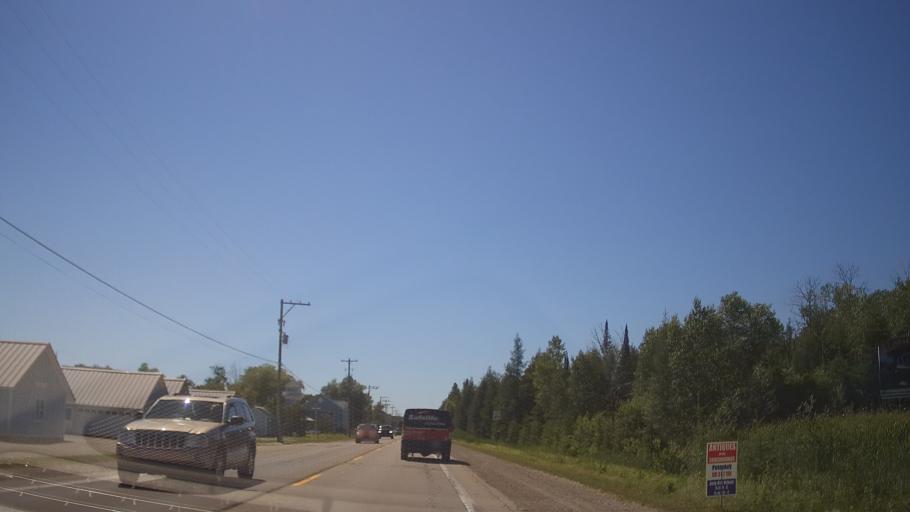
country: US
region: Michigan
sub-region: Emmet County
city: Petoskey
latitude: 45.4239
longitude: -84.8398
